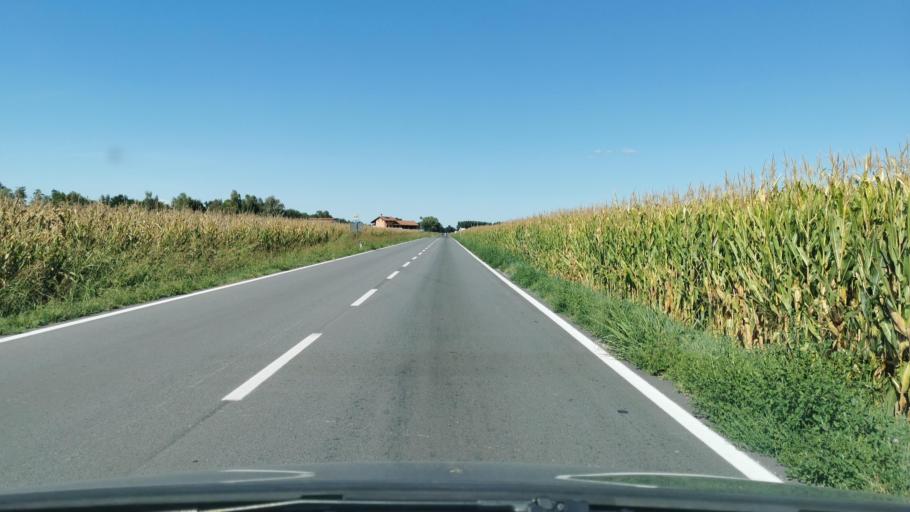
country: IT
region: Piedmont
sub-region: Provincia di Cuneo
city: Genola
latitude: 44.5675
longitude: 7.6295
